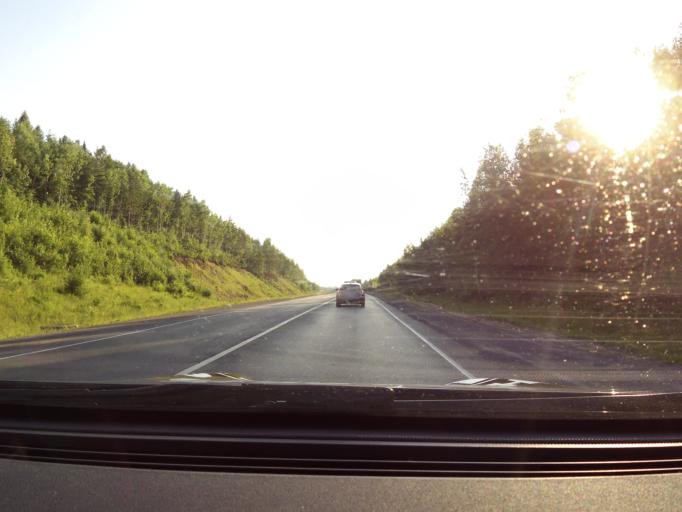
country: RU
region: Sverdlovsk
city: Druzhinino
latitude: 56.8273
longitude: 59.5932
